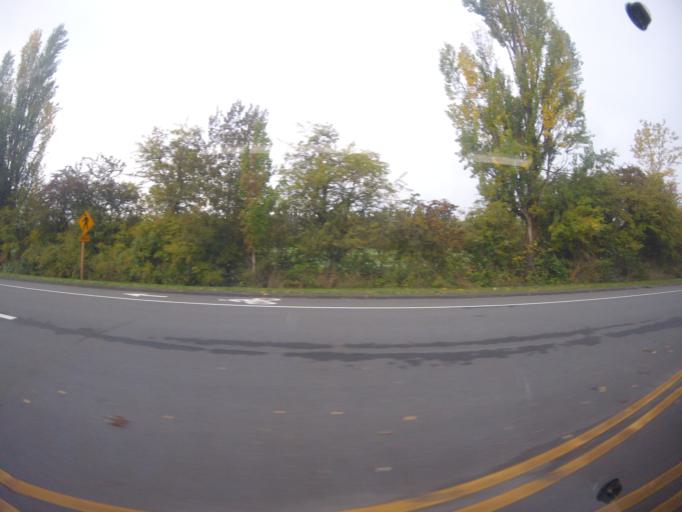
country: US
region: Washington
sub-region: King County
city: Medina
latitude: 47.6285
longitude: -122.2280
